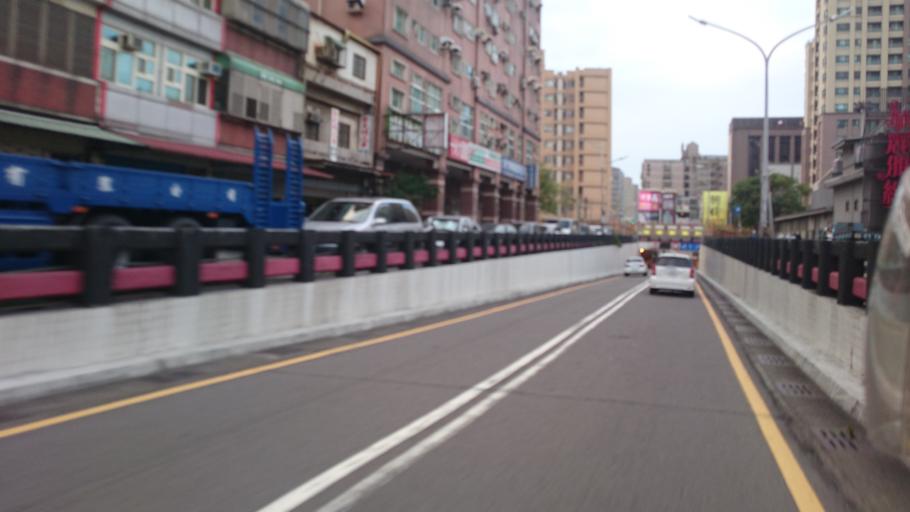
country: TW
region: Taiwan
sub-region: Hsinchu
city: Hsinchu
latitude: 24.8040
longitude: 120.9785
